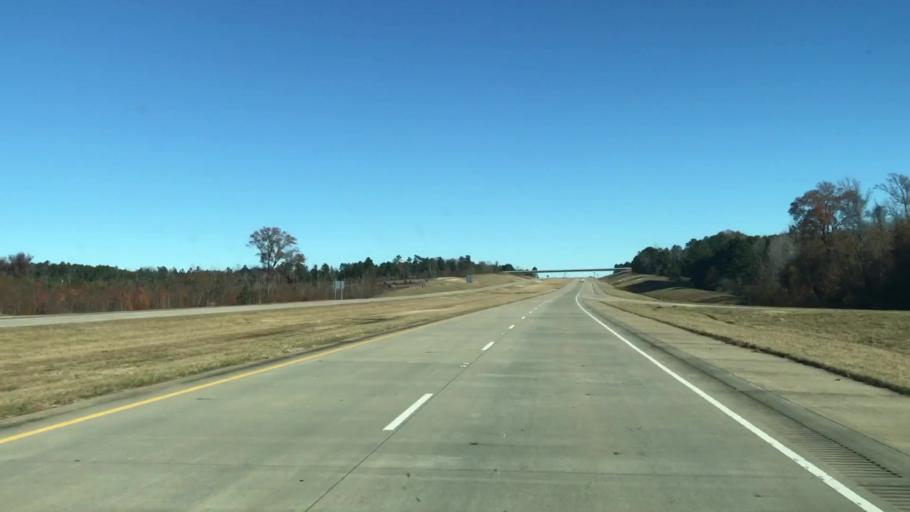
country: US
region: Louisiana
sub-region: Caddo Parish
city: Vivian
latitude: 33.0003
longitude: -93.9082
